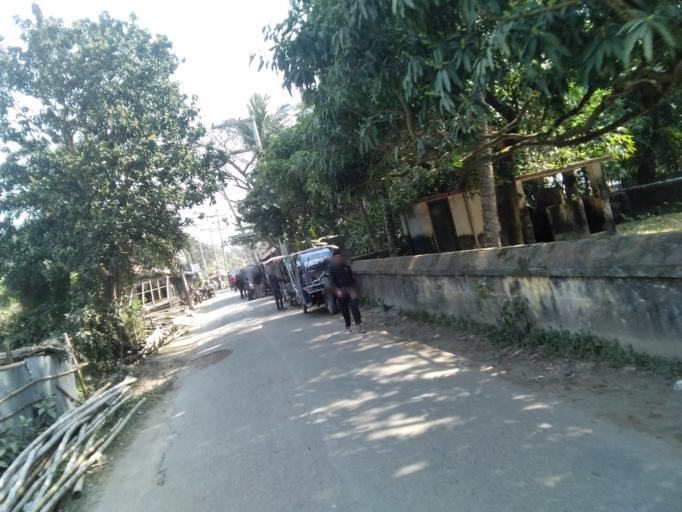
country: IN
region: West Bengal
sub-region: North 24 Parganas
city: Taki
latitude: 22.5900
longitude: 88.9991
